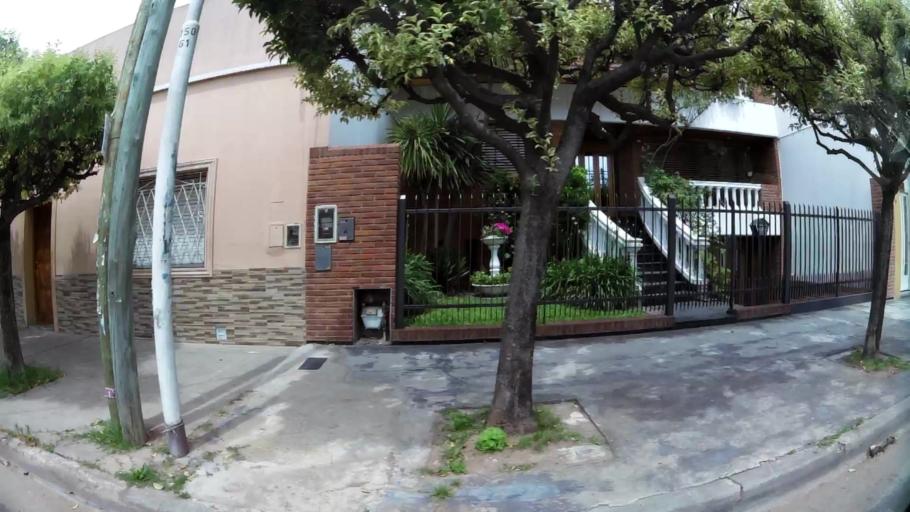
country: AR
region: Buenos Aires
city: San Justo
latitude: -34.6724
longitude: -58.5455
